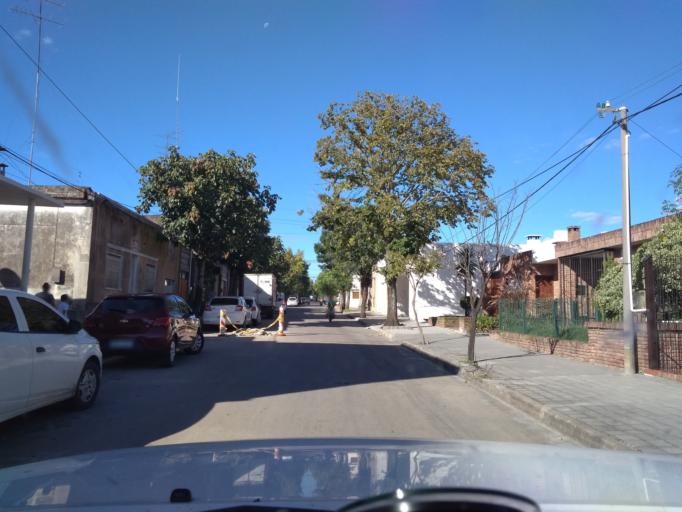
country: UY
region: Florida
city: Florida
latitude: -34.0990
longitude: -56.2193
